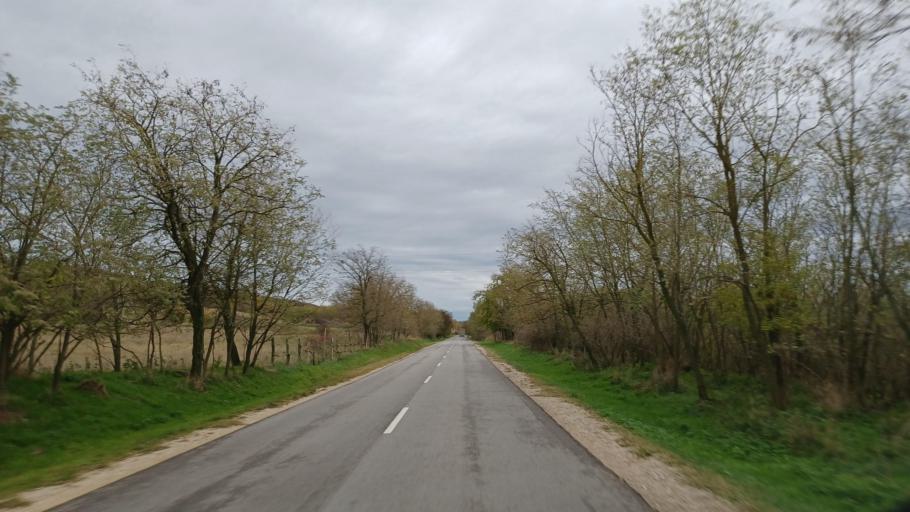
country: HU
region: Tolna
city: Pincehely
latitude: 46.6219
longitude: 18.4171
